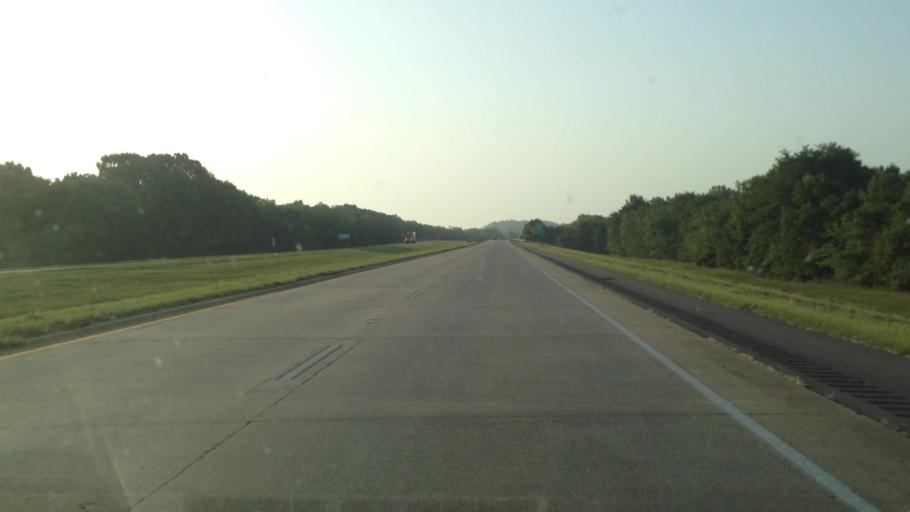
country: US
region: Louisiana
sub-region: Grant Parish
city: Colfax
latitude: 31.5039
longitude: -92.8789
